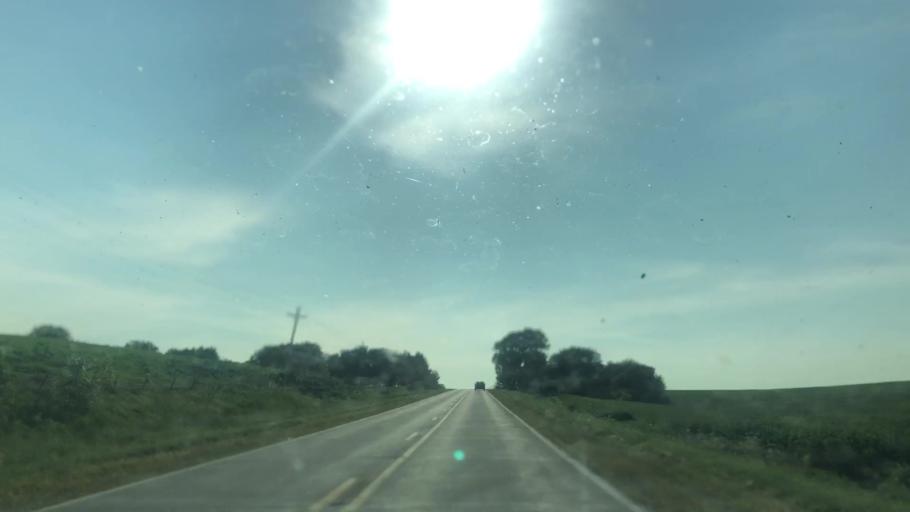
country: US
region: Iowa
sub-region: Marshall County
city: Marshalltown
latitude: 42.0490
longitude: -92.9726
